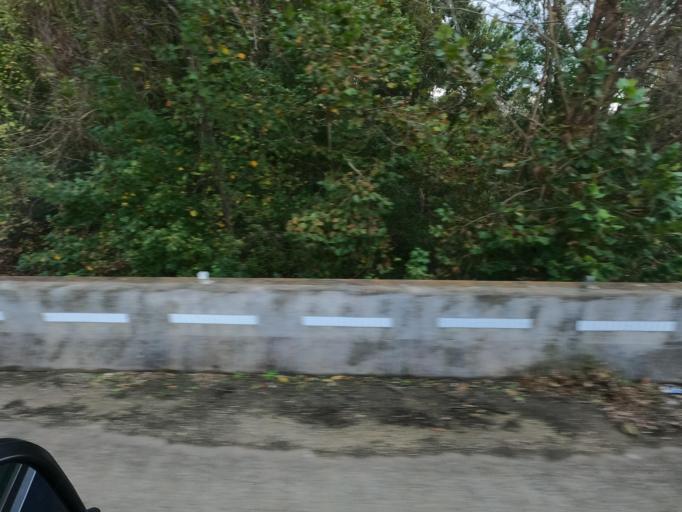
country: US
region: Tennessee
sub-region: Cheatham County
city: Pegram
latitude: 36.1071
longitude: -87.0734
